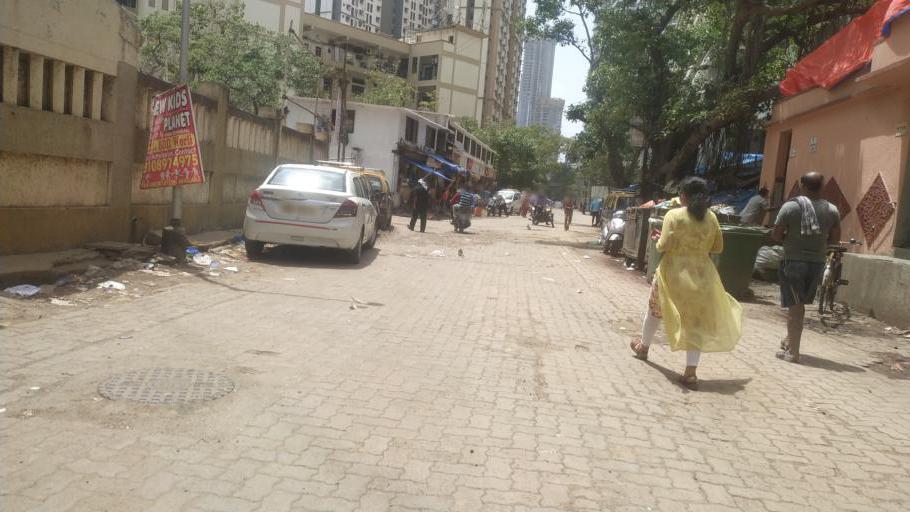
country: IN
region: Maharashtra
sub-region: Mumbai Suburban
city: Mumbai
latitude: 19.0007
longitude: 72.8256
